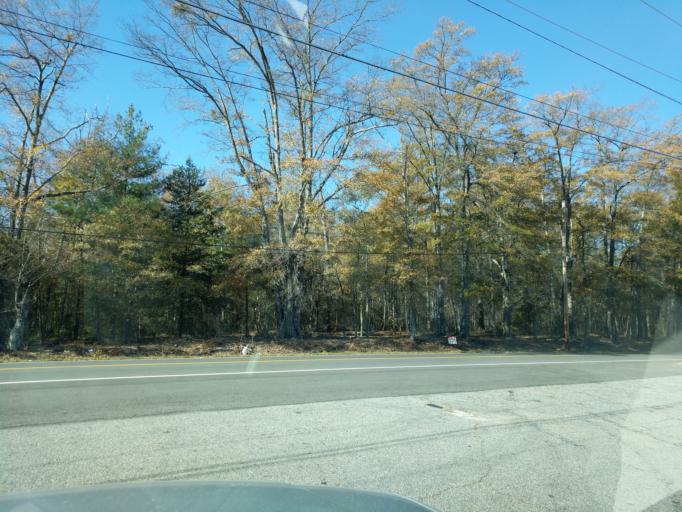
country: US
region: South Carolina
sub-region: Spartanburg County
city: Lyman
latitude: 34.9569
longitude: -82.1432
